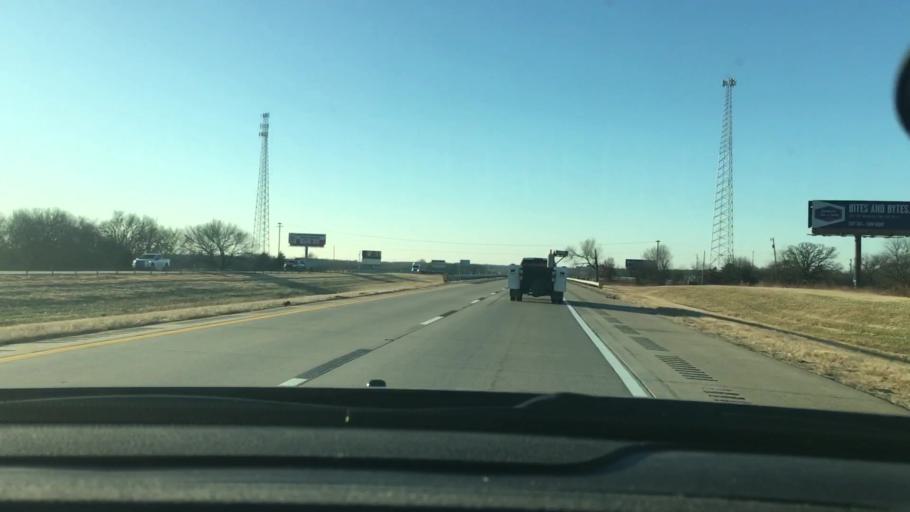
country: US
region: Oklahoma
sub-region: Carter County
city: Ardmore
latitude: 34.2773
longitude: -97.1614
